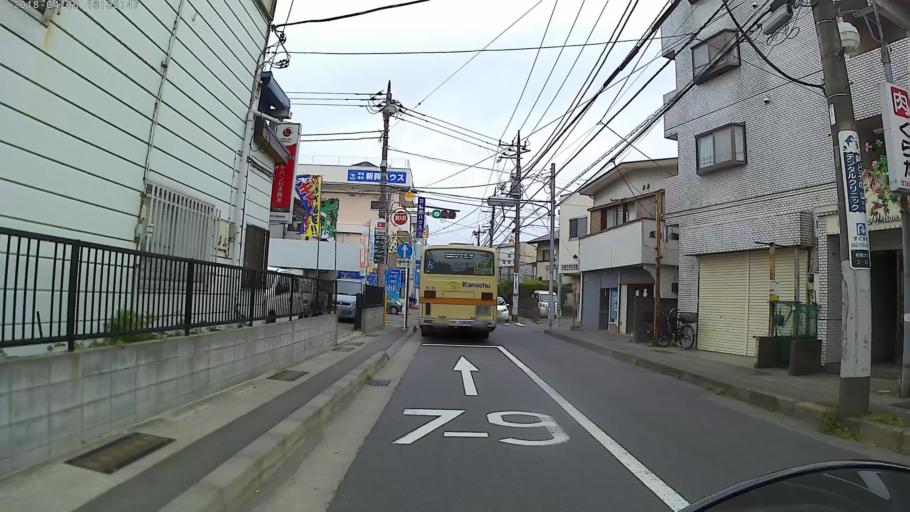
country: JP
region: Kanagawa
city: Minami-rinkan
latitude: 35.5118
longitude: 139.4228
